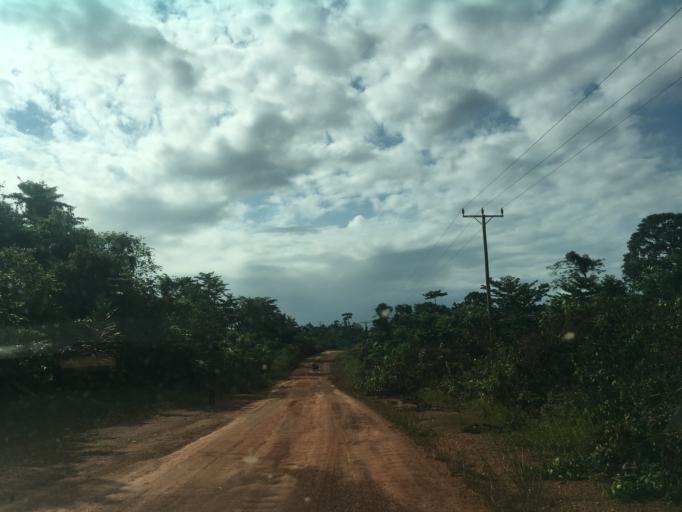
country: GH
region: Western
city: Wassa-Akropong
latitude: 5.9129
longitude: -2.4049
